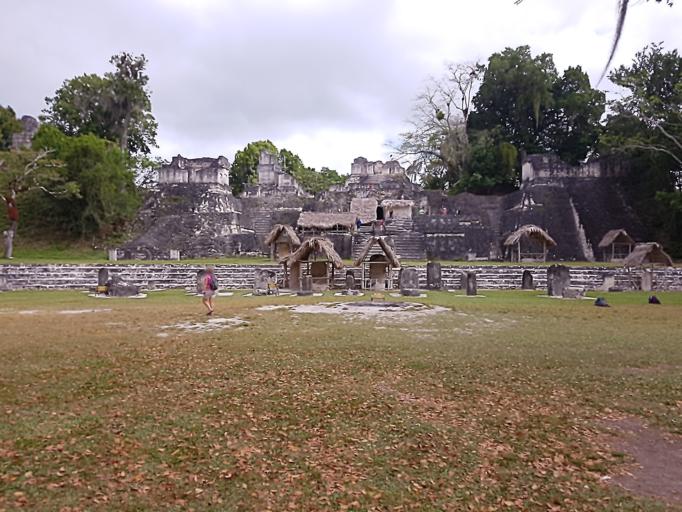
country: GT
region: Peten
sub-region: Municipio de San Jose
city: San Jose
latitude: 17.2219
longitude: -89.6236
